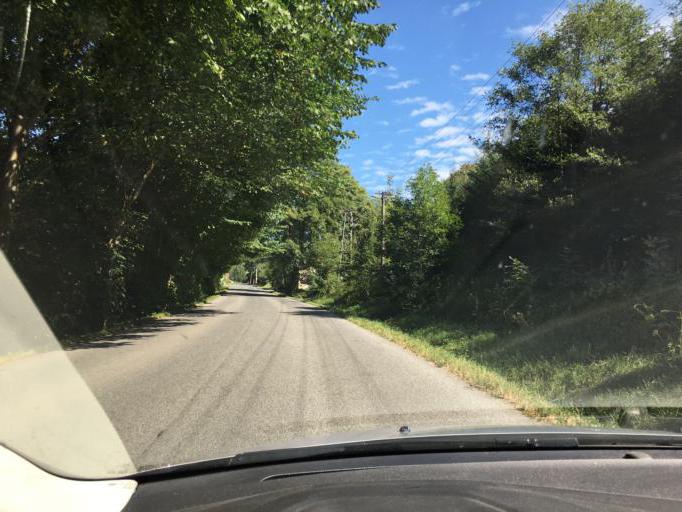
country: CZ
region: Liberecky
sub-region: Okres Semily
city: Vysoke nad Jizerou
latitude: 50.6599
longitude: 15.4162
